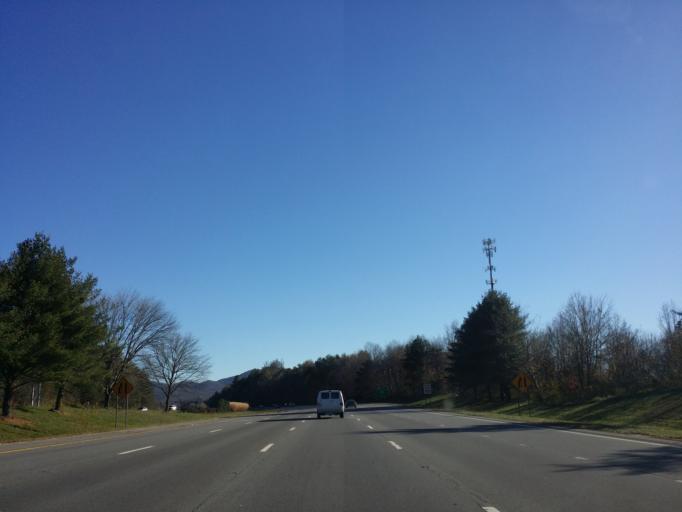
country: US
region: North Carolina
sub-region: Buncombe County
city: Asheville
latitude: 35.5923
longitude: -82.5285
